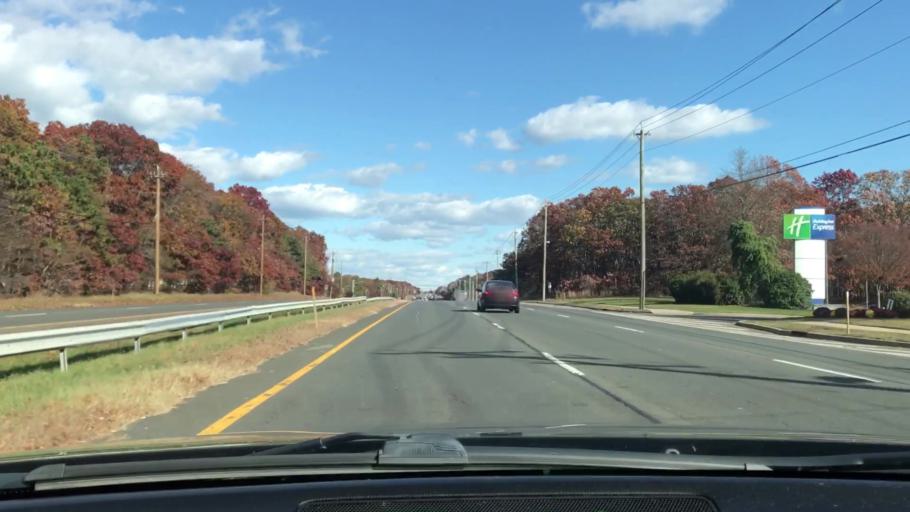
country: US
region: New York
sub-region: Suffolk County
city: Centereach
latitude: 40.8888
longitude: -73.0972
